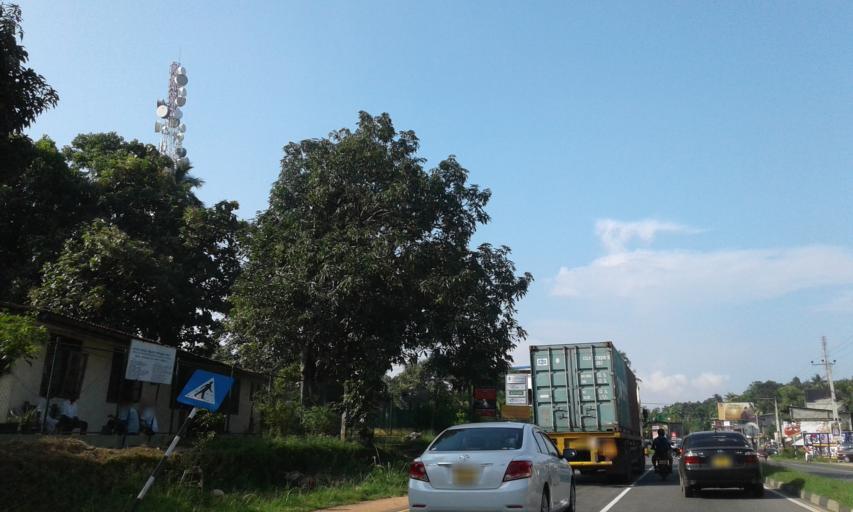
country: LK
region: Western
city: Gampaha
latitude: 7.0211
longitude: 79.9735
